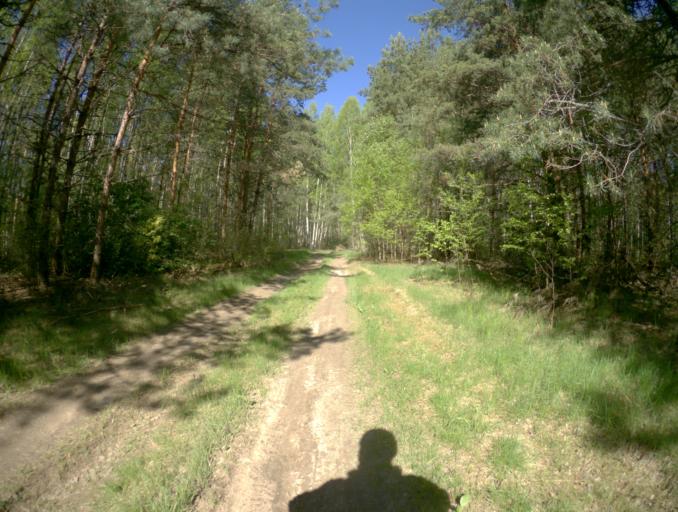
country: RU
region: Rjazan
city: Spas-Klepiki
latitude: 55.2497
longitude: 40.1100
